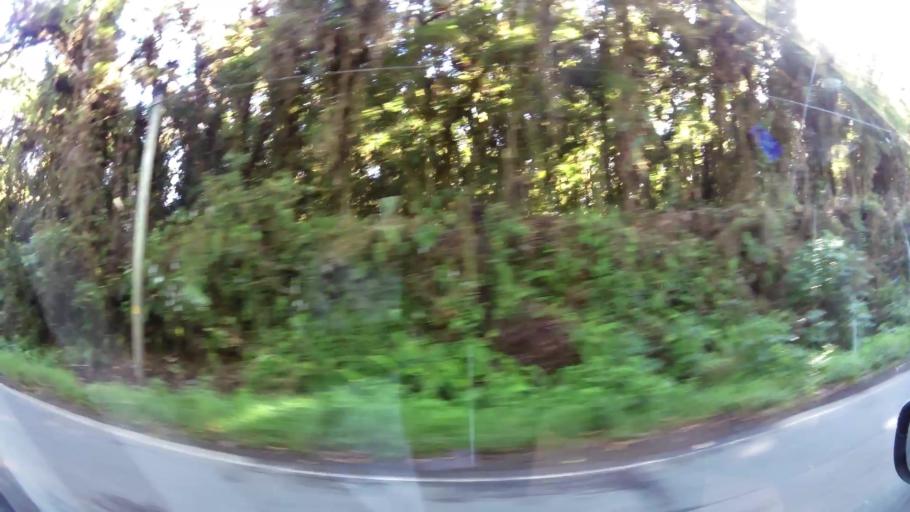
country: CR
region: San Jose
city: San Marcos
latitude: 9.7009
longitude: -83.9439
